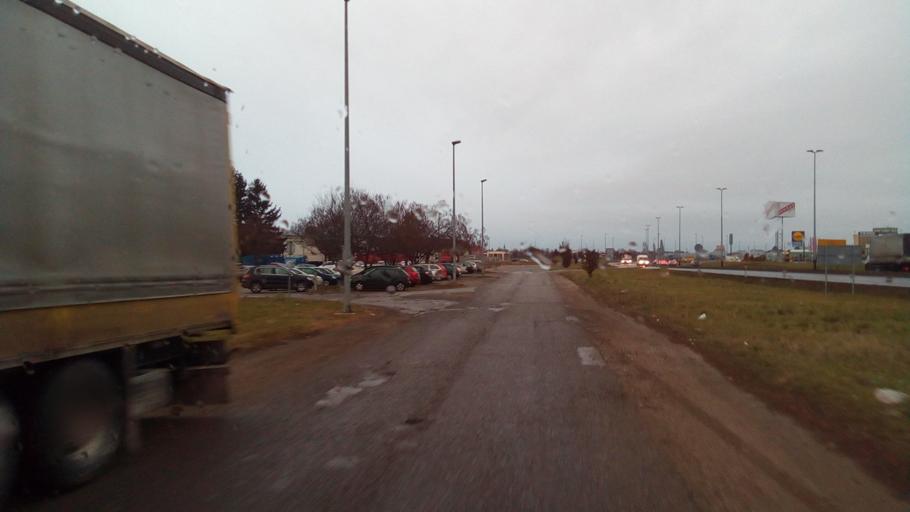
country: HR
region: Varazdinska
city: Varazdin
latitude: 46.2881
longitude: 16.3529
